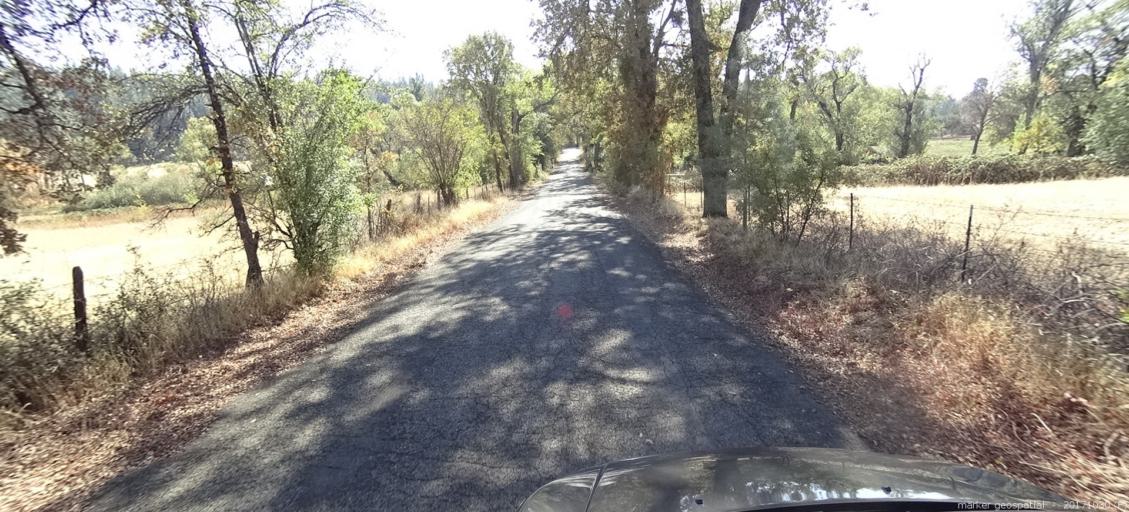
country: US
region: California
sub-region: Shasta County
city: Shingletown
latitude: 40.5154
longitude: -121.9741
